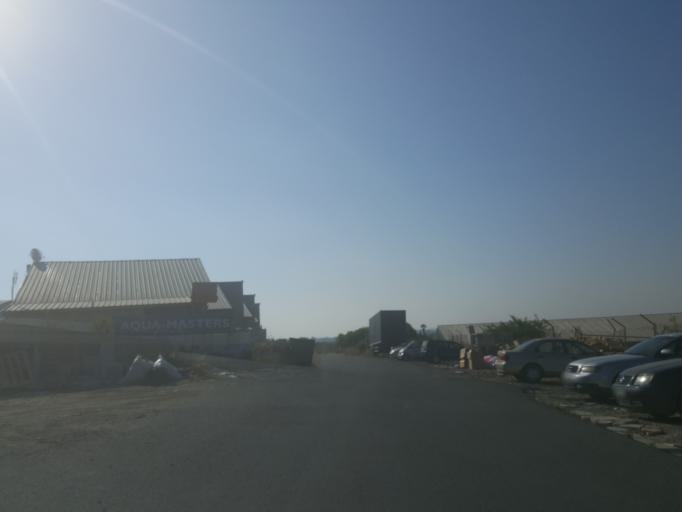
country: CY
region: Lefkosia
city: Nicosia
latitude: 35.1230
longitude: 33.3587
